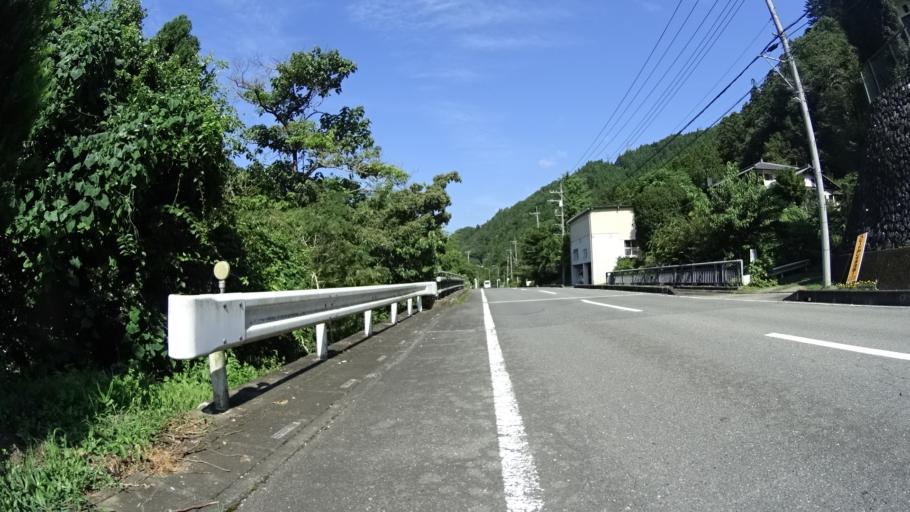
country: JP
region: Saitama
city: Chichibu
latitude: 36.0265
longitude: 138.9507
